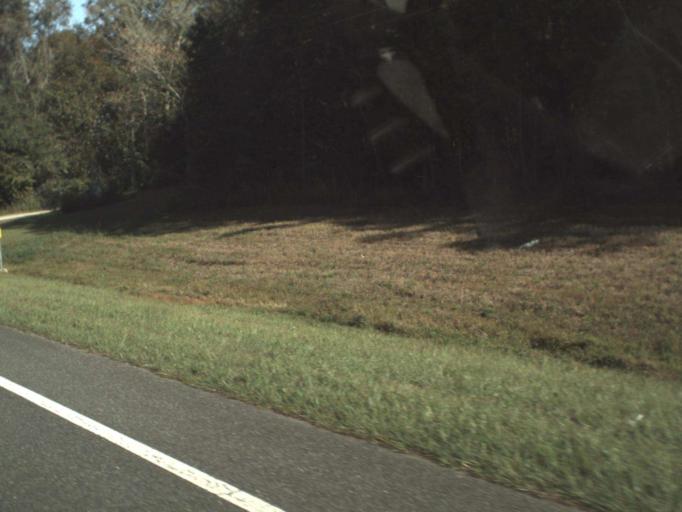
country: US
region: Florida
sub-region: Gadsden County
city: Midway
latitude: 30.5275
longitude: -84.4713
